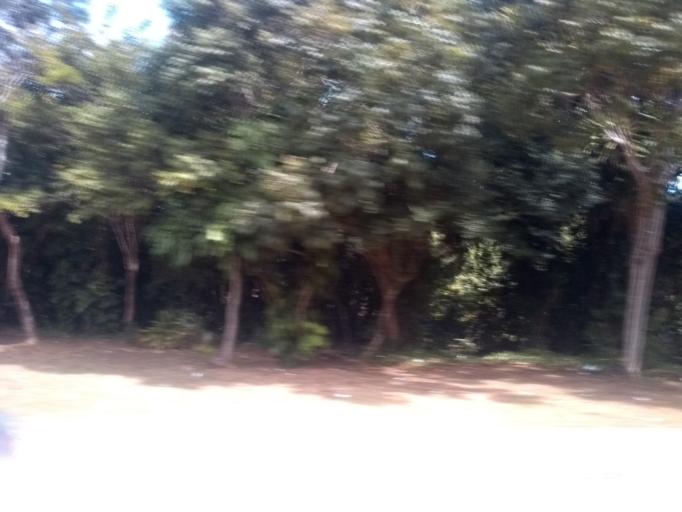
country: BR
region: Bahia
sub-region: Salvador
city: Salvador
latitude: -12.9447
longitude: -38.4266
